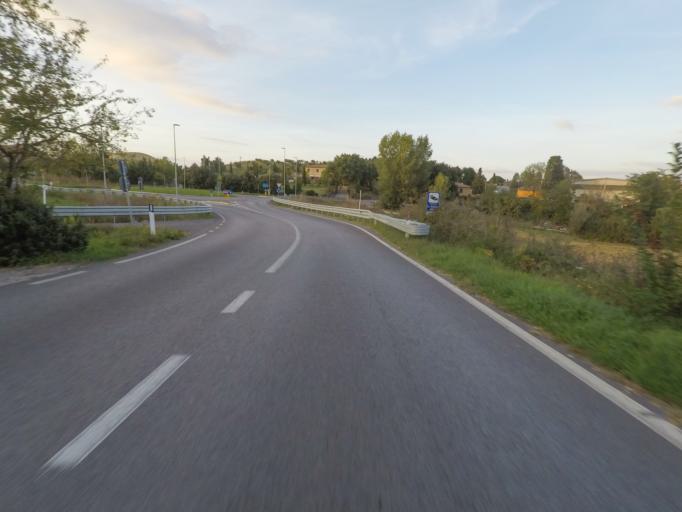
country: IT
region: Tuscany
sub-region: Provincia di Siena
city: Pienza
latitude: 43.0838
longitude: 11.6767
